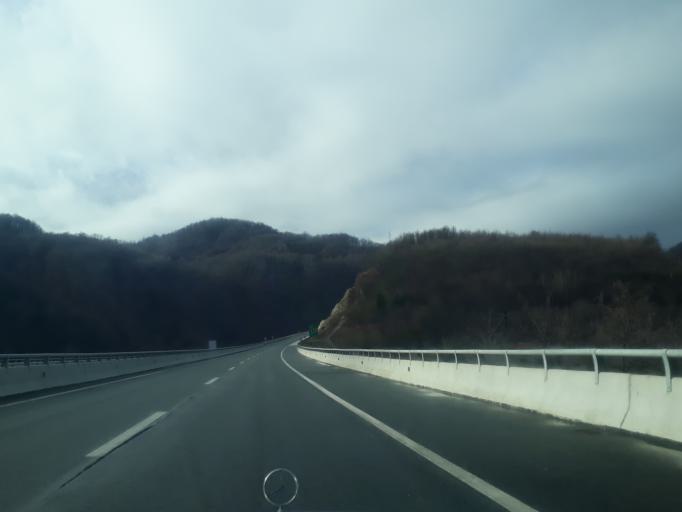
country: BA
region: Federation of Bosnia and Herzegovina
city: Polje
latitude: 43.8354
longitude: 18.1160
